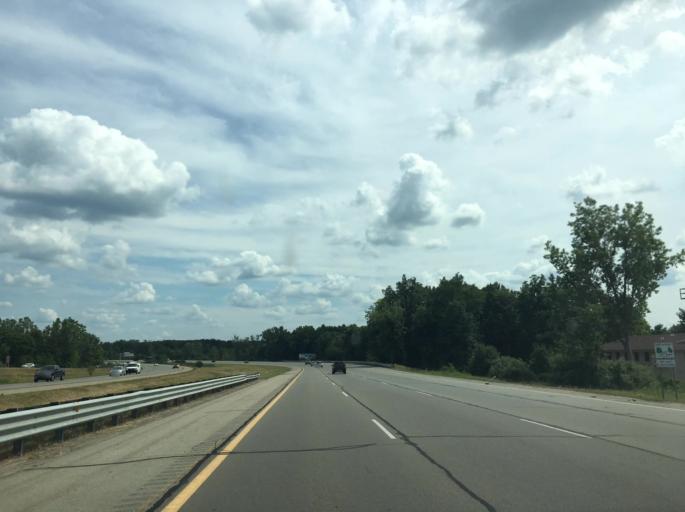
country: US
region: Michigan
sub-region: Oakland County
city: Holly
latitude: 42.8149
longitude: -83.5699
